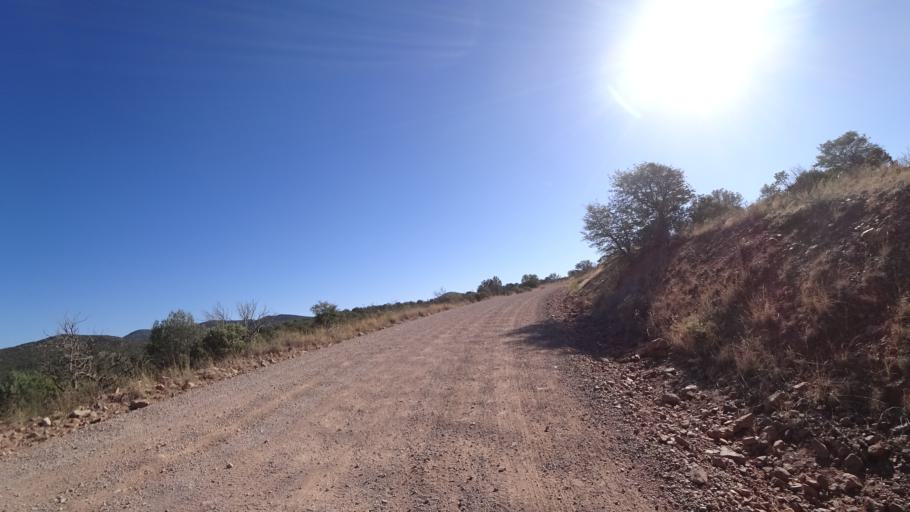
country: US
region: Arizona
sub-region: Cochise County
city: Huachuca City
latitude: 31.5314
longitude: -110.5308
